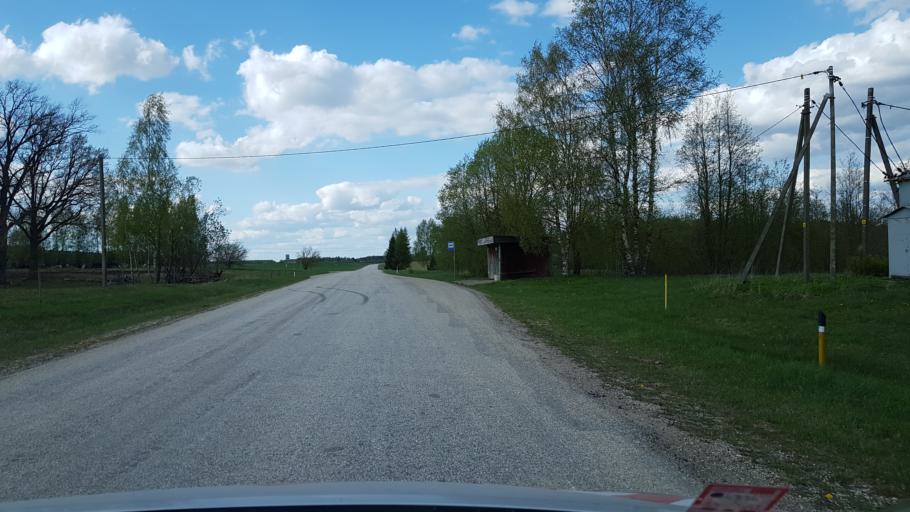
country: EE
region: Tartu
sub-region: UElenurme vald
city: Ulenurme
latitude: 58.2686
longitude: 26.9095
